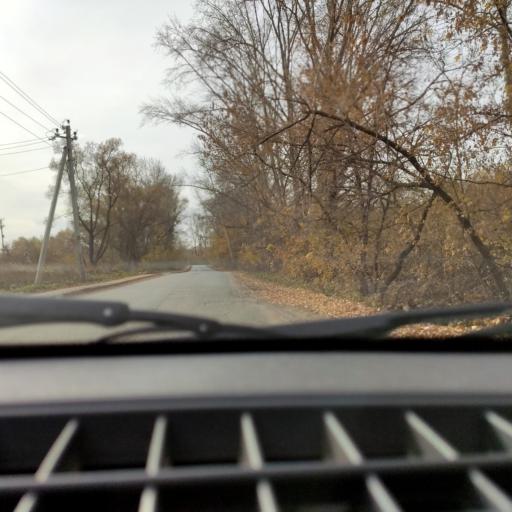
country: RU
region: Bashkortostan
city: Ufa
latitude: 54.6944
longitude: 55.9677
